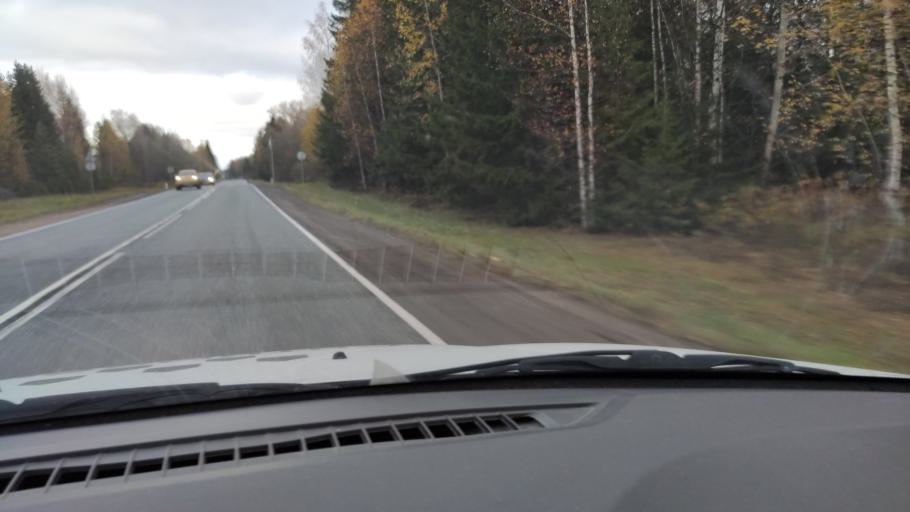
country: RU
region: Kirov
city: Belaya Kholunitsa
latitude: 58.8454
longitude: 50.7072
